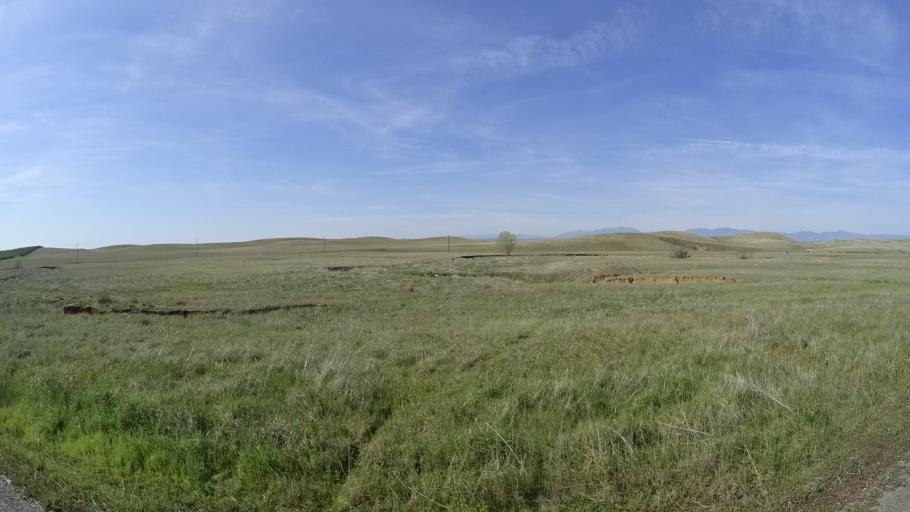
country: US
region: California
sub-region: Glenn County
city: Willows
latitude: 39.6138
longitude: -122.2905
